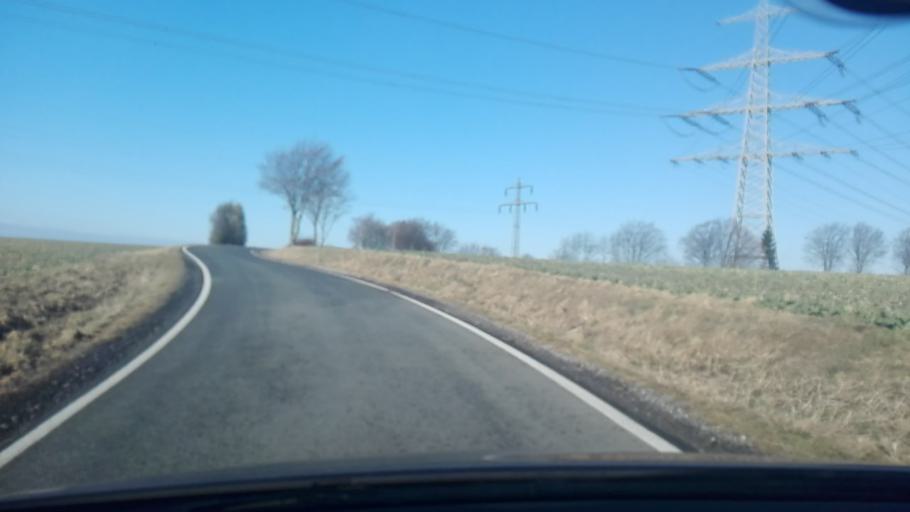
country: DE
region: North Rhine-Westphalia
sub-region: Regierungsbezirk Arnsberg
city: Unna
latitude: 51.5174
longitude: 7.7375
